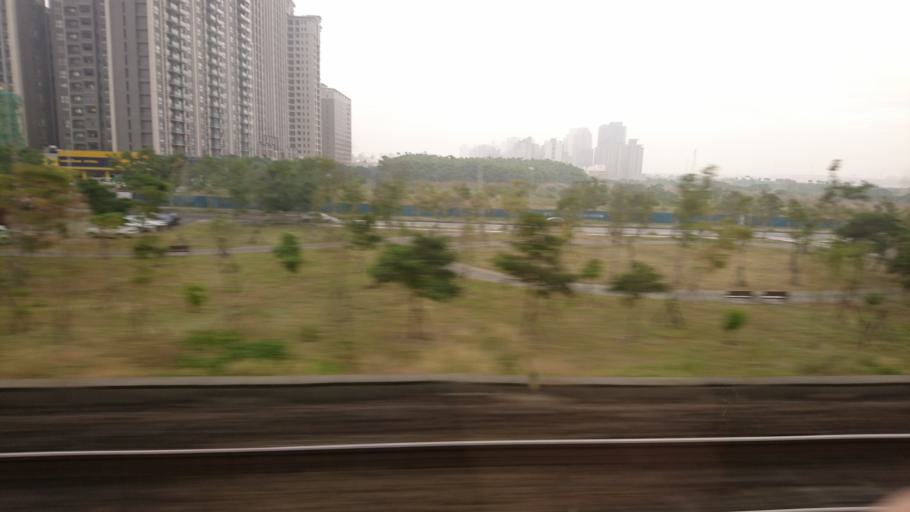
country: TW
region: Taiwan
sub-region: Hsinchu
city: Zhubei
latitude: 24.8267
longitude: 121.0005
